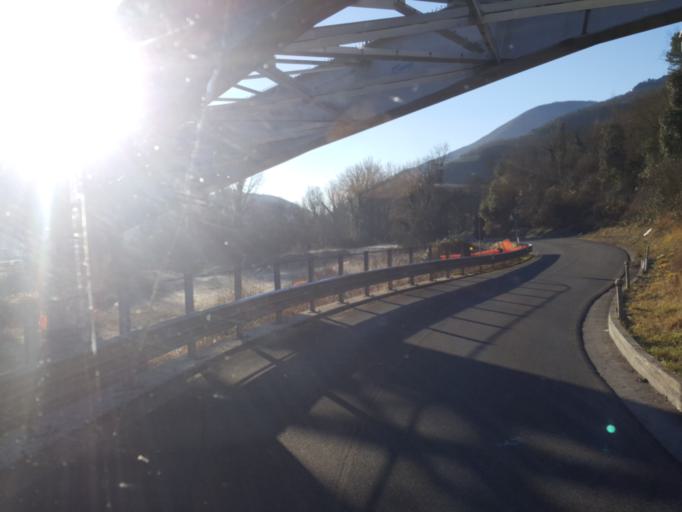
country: IT
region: Latium
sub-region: Provincia di Rieti
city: Colli sul Velino
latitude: 42.5255
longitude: 12.7333
